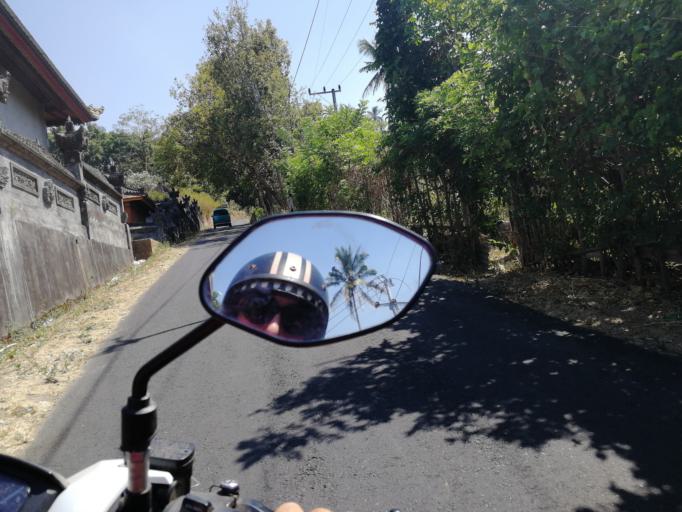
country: ID
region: Bali
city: Banjar Kedisan
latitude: -8.1540
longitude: 115.3077
